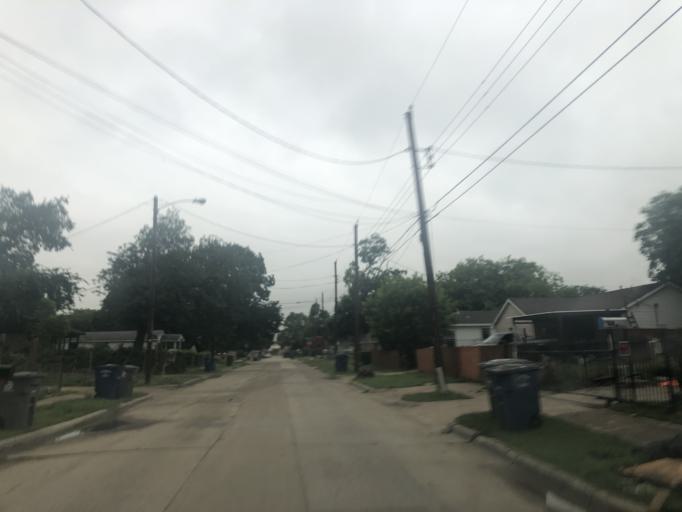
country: US
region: Texas
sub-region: Dallas County
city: Cockrell Hill
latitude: 32.7828
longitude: -96.8797
